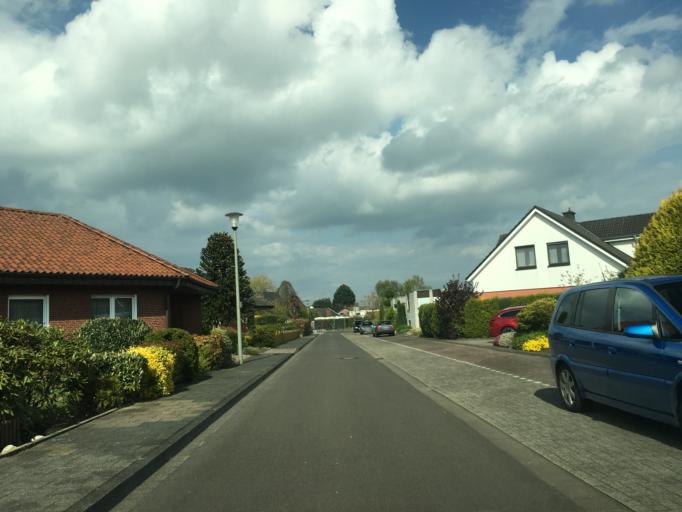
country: DE
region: North Rhine-Westphalia
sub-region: Regierungsbezirk Munster
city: Steinfurt
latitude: 52.1349
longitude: 7.3322
